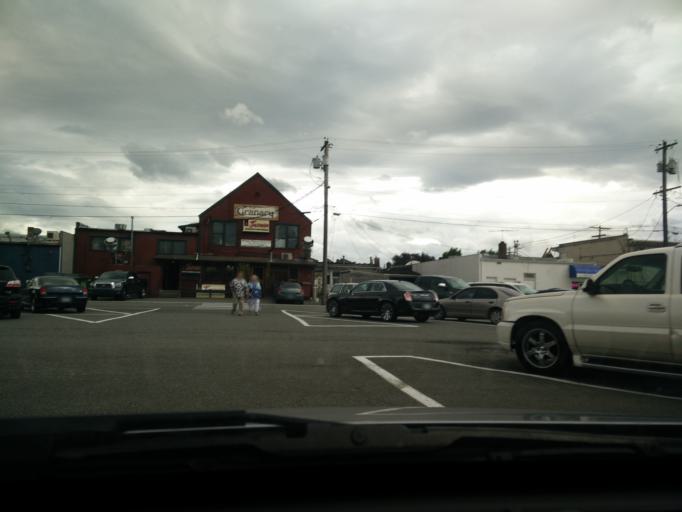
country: US
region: Washington
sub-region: Snohomish County
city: Stanwood
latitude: 48.2429
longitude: -122.3513
